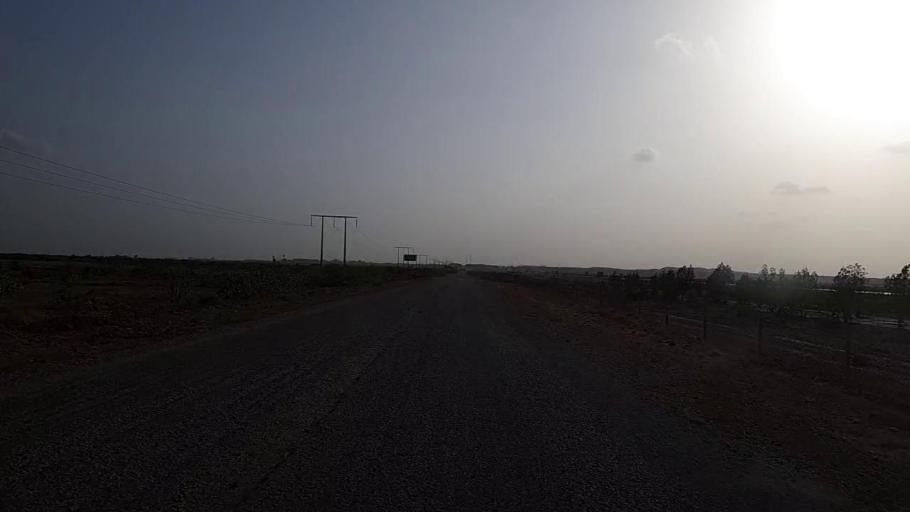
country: PK
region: Sindh
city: Thatta
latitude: 25.1904
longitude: 67.8498
